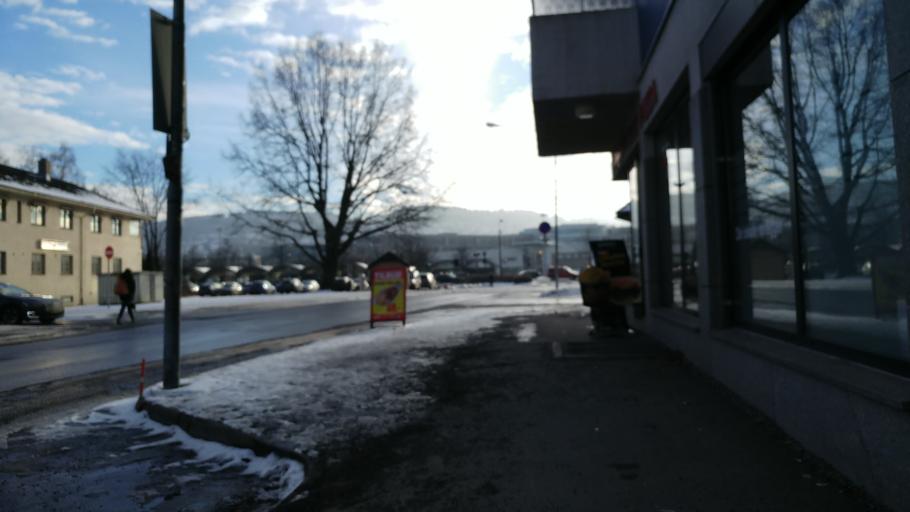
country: NO
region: Akershus
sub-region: Skedsmo
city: Lillestrom
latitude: 59.9553
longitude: 11.0425
